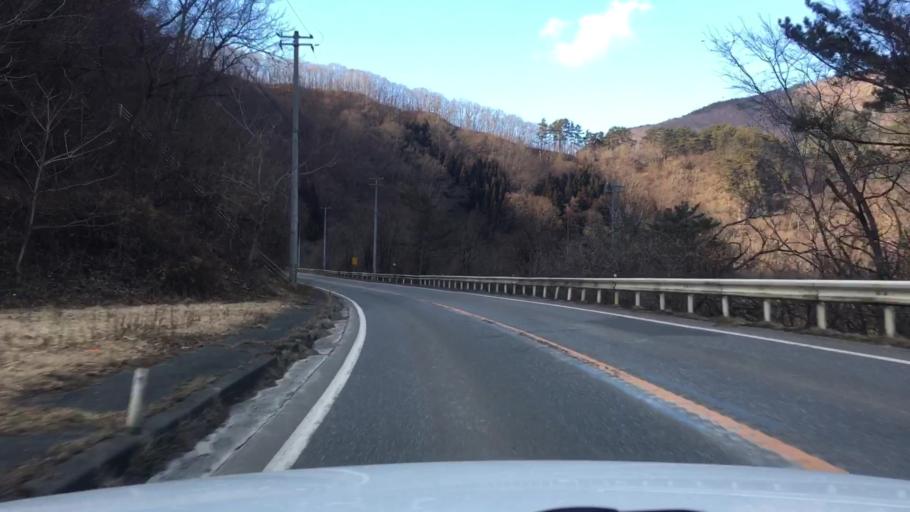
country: JP
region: Iwate
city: Tono
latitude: 39.6195
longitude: 141.6224
